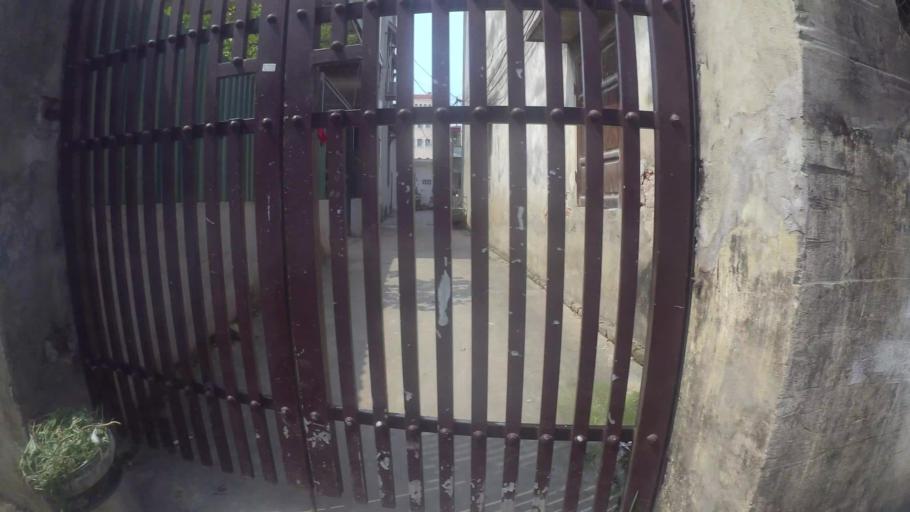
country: VN
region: Ha Noi
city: Tay Ho
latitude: 21.0873
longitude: 105.7970
